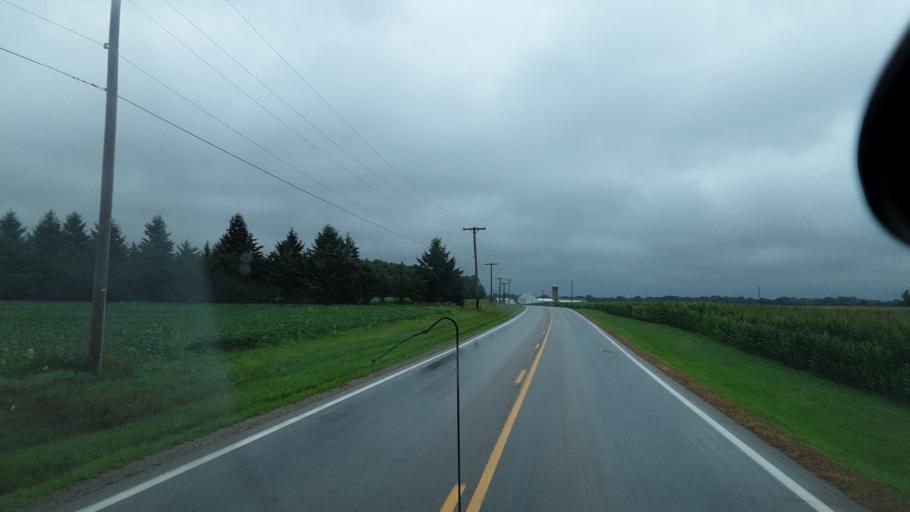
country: US
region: Ohio
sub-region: Mercer County
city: Rockford
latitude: 40.7478
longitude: -84.7717
